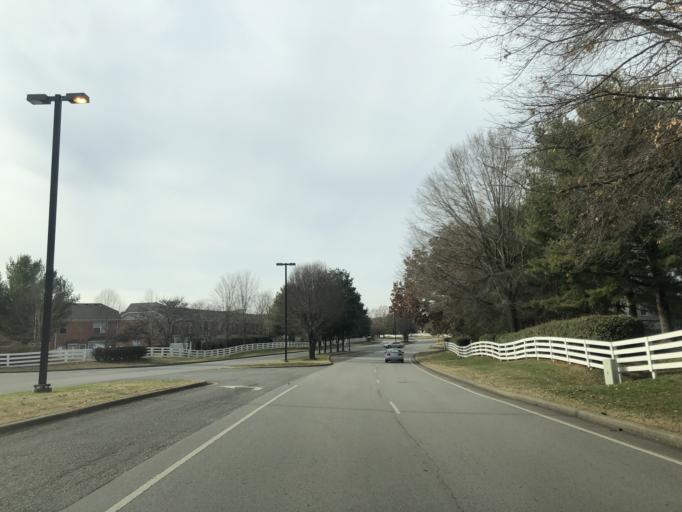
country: US
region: Tennessee
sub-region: Williamson County
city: Franklin
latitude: 35.9634
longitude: -86.8861
